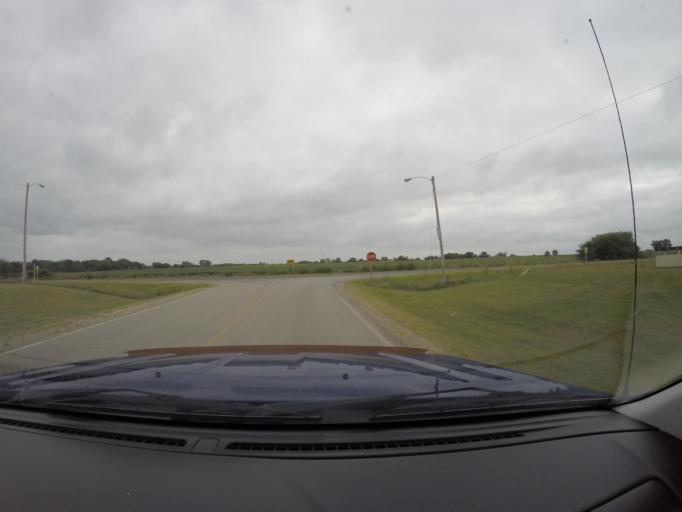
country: US
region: Kansas
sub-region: Morris County
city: Council Grove
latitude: 38.8554
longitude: -96.4898
